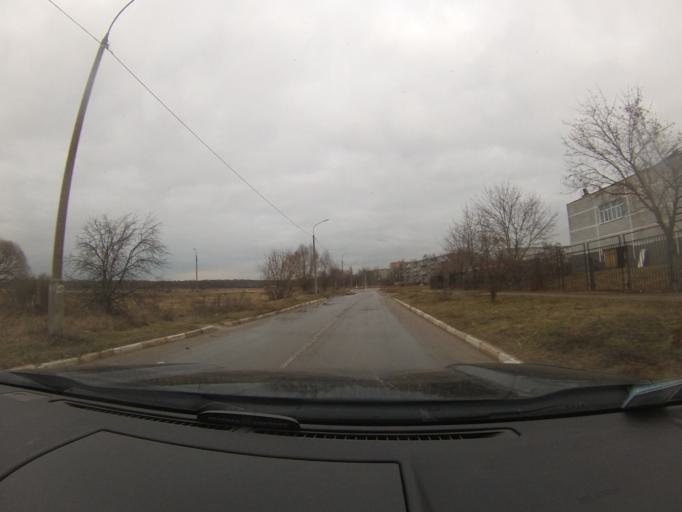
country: RU
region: Moskovskaya
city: Lopatinskiy
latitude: 55.3379
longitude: 38.7099
